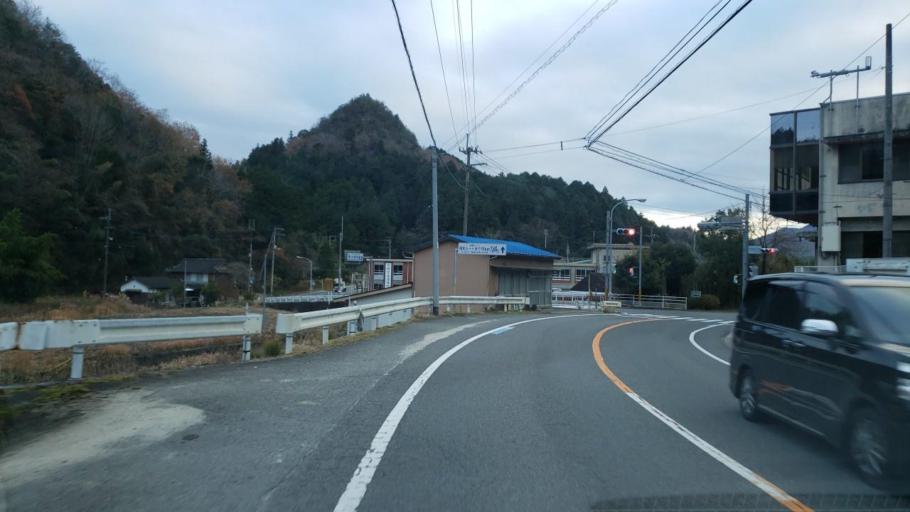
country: JP
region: Tokushima
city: Wakimachi
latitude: 34.1875
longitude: 134.1710
